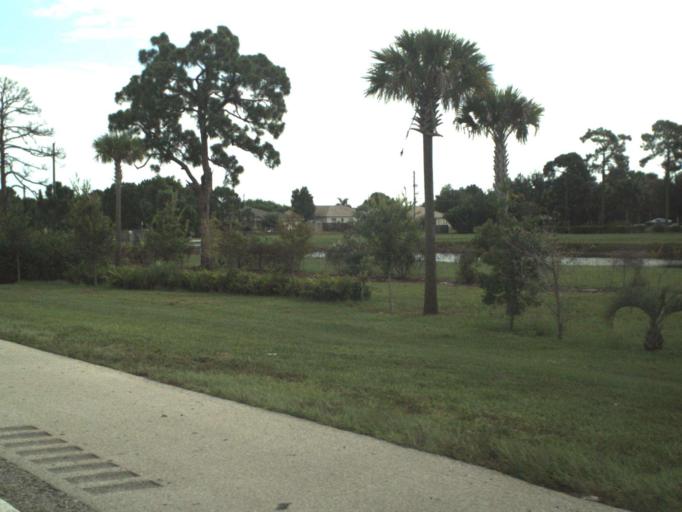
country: US
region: Florida
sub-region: Saint Lucie County
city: River Park
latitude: 27.3366
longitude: -80.4140
